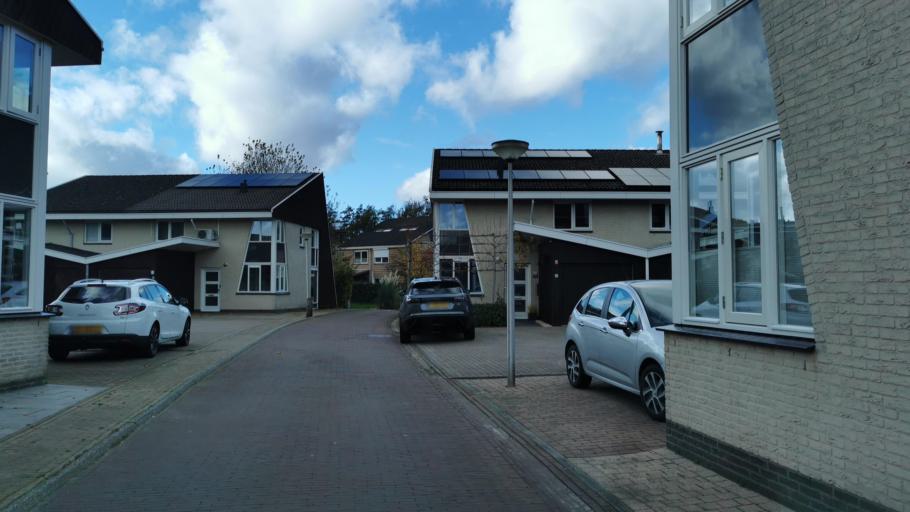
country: DE
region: North Rhine-Westphalia
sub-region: Regierungsbezirk Munster
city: Gronau
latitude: 52.2068
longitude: 6.9719
